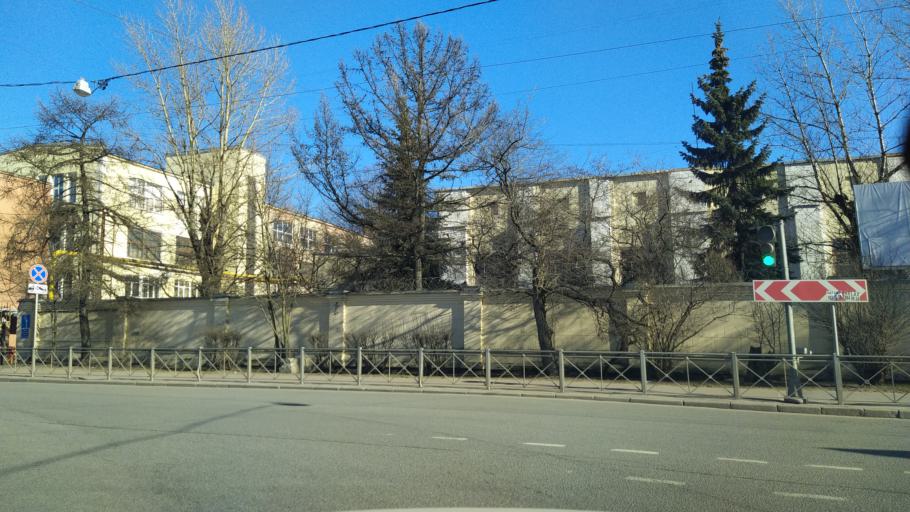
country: RU
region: St.-Petersburg
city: Centralniy
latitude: 59.9003
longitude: 30.3724
